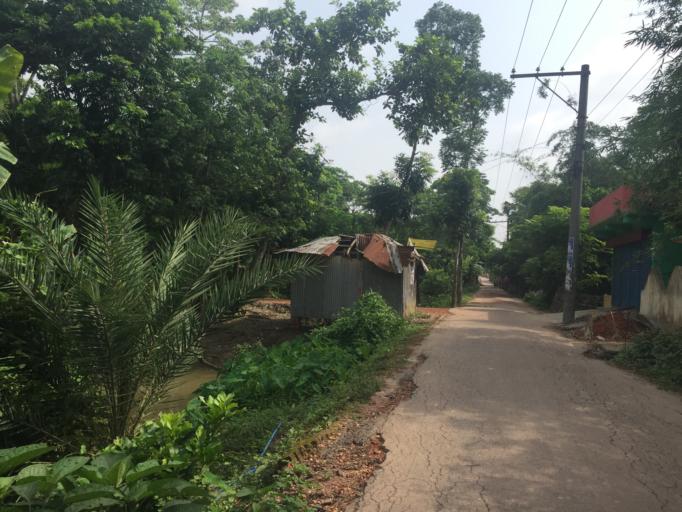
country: BD
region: Barisal
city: Mathba
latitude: 22.2147
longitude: 89.9131
